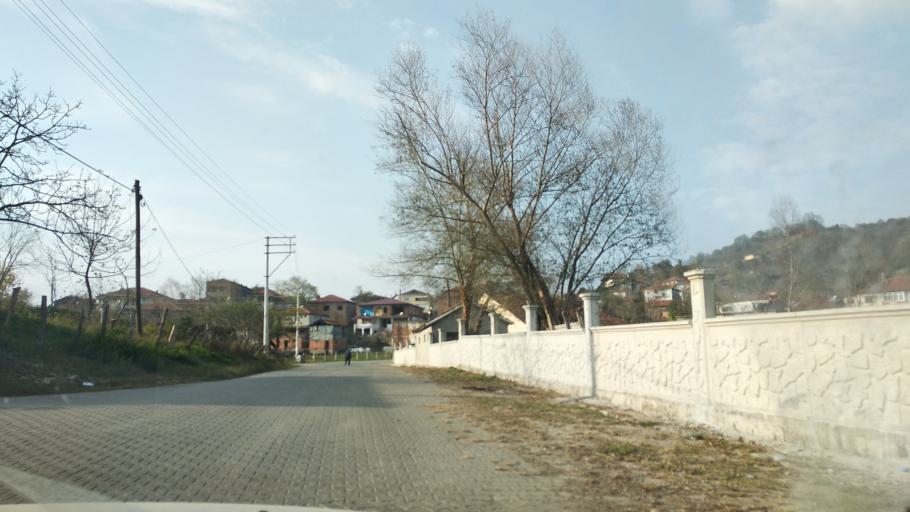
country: TR
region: Sakarya
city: Karasu
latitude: 41.0547
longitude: 30.6295
